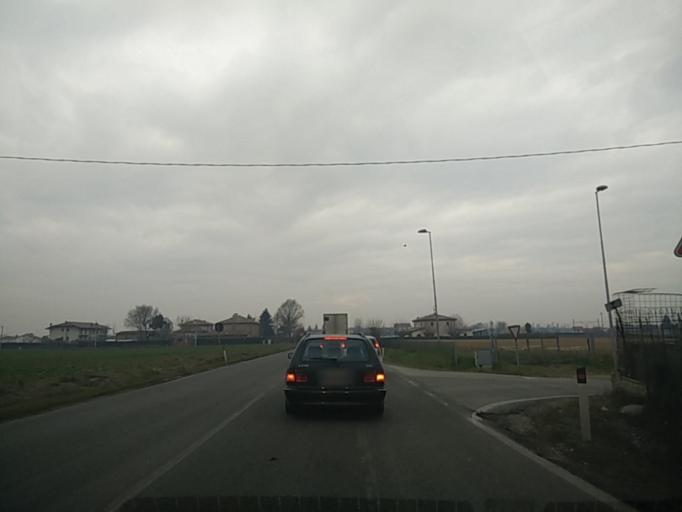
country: IT
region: Emilia-Romagna
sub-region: Provincia di Rimini
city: Santa Giustina
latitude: 44.0698
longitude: 12.5017
